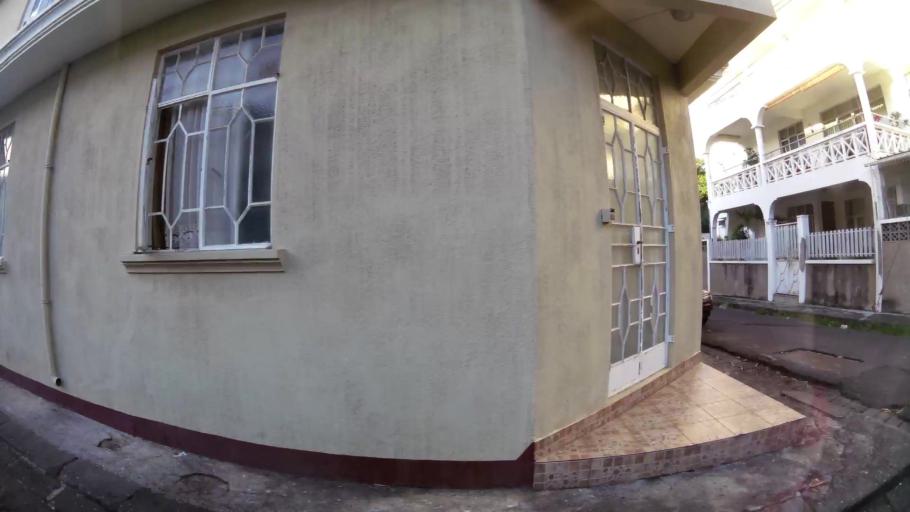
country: MU
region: Port Louis
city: Port Louis
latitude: -20.1707
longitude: 57.4999
